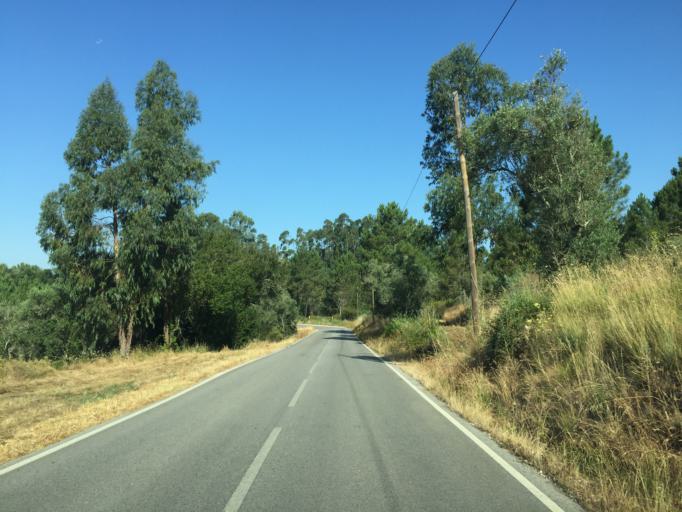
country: PT
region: Santarem
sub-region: Ferreira do Zezere
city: Ferreira do Zezere
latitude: 39.6028
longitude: -8.3105
